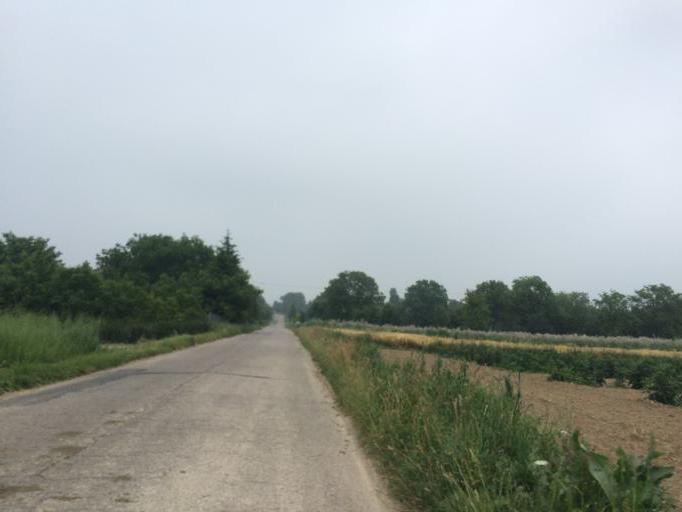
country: PL
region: Lublin Voivodeship
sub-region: Powiat pulawski
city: Markuszow
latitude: 51.3603
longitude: 22.2647
